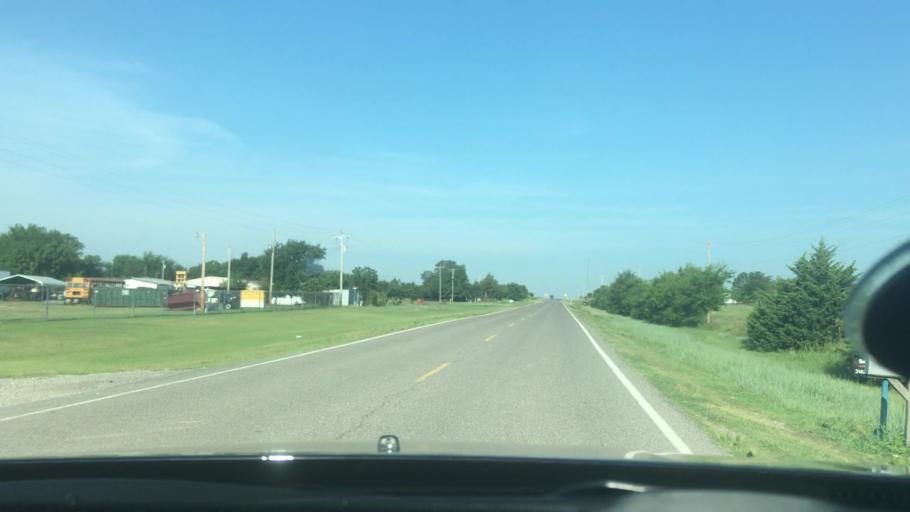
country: US
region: Oklahoma
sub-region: Garvin County
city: Wynnewood
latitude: 34.6518
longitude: -97.2377
